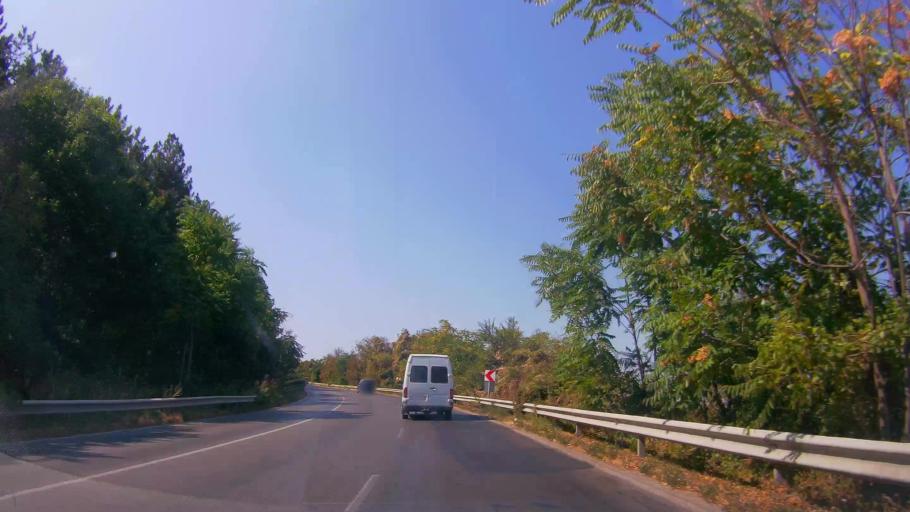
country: BG
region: Razgrad
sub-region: Obshtina Tsar Kaloyan
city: Tsar Kaloyan
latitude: 43.6273
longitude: 26.2115
